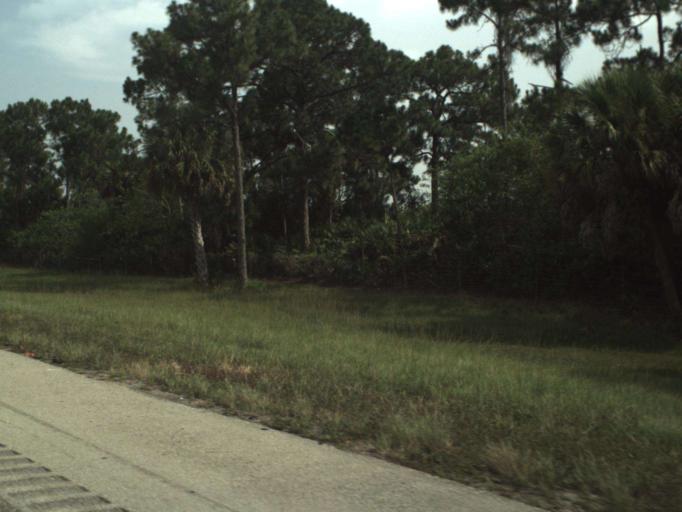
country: US
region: Florida
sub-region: Saint Lucie County
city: Port Saint Lucie
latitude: 27.2312
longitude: -80.4062
